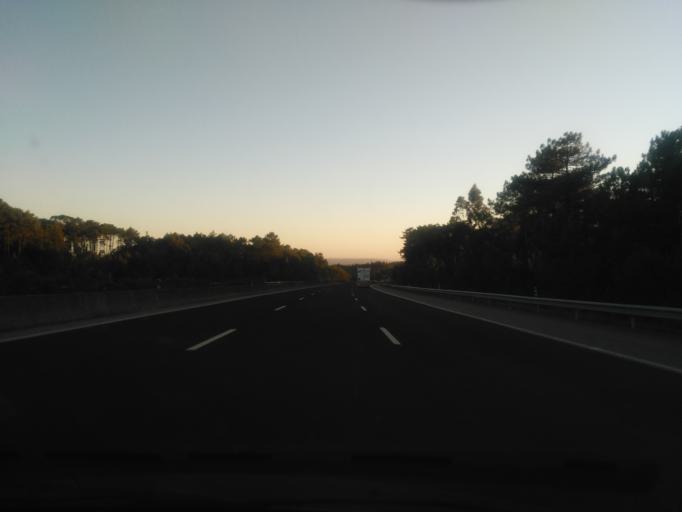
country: PT
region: Leiria
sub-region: Leiria
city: Maceira
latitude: 39.6822
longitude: -8.9366
